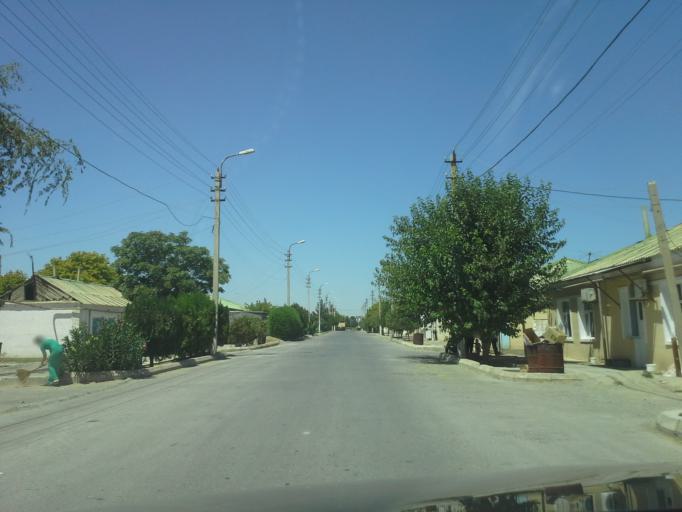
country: TM
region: Ahal
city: Abadan
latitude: 38.0175
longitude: 58.2630
